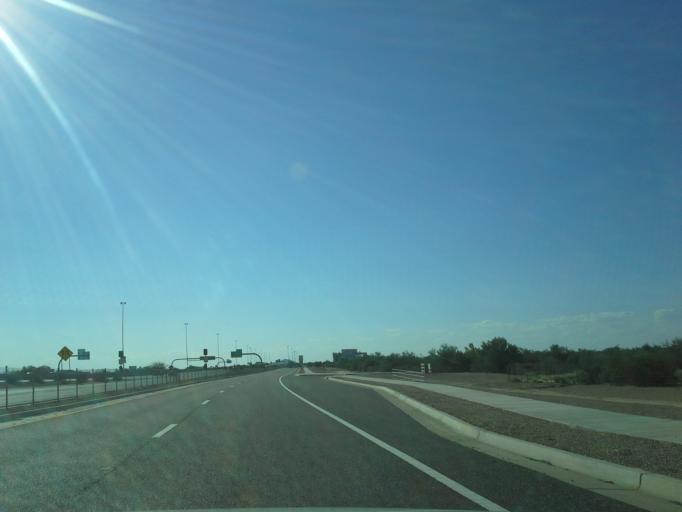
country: US
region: Arizona
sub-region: Maricopa County
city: Paradise Valley
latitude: 33.6557
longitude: -111.9113
